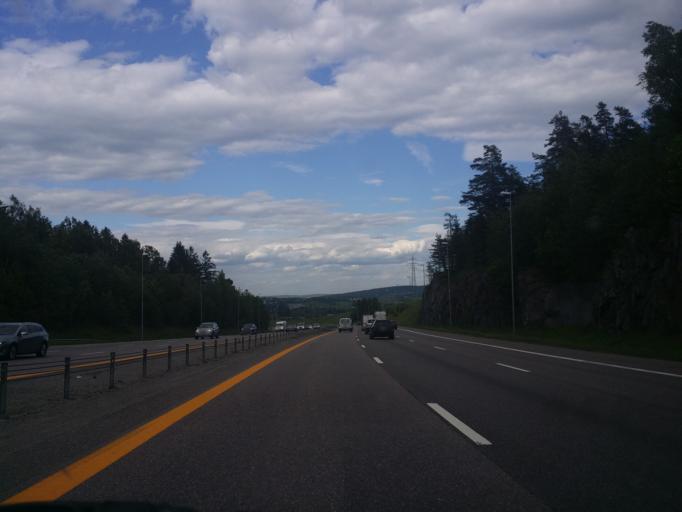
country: NO
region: Akershus
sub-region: Lorenskog
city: Kjenn
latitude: 59.9625
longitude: 10.9763
